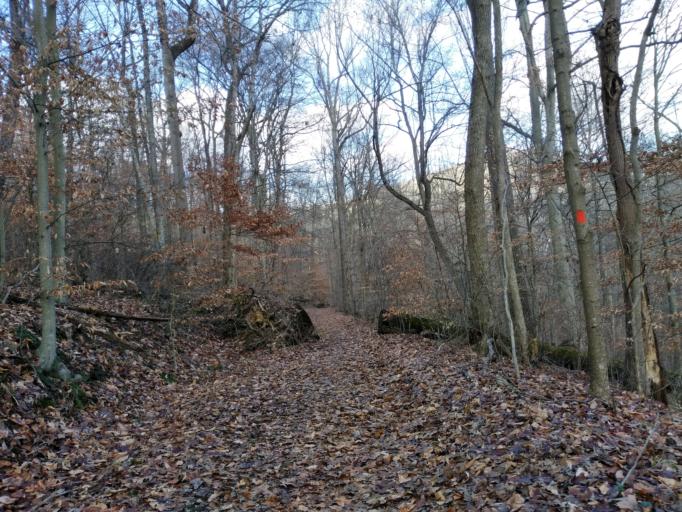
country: US
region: Ohio
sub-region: Fairfield County
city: Lancaster
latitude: 39.6461
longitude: -82.6444
